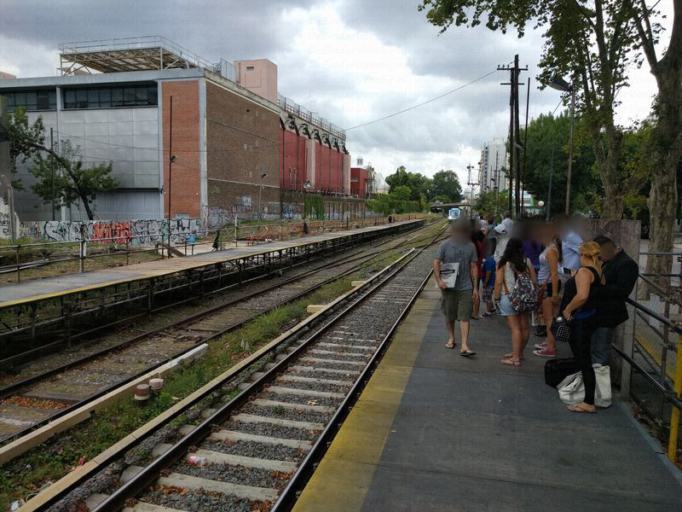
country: AR
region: Buenos Aires F.D.
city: Colegiales
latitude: -34.5749
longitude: -58.4466
